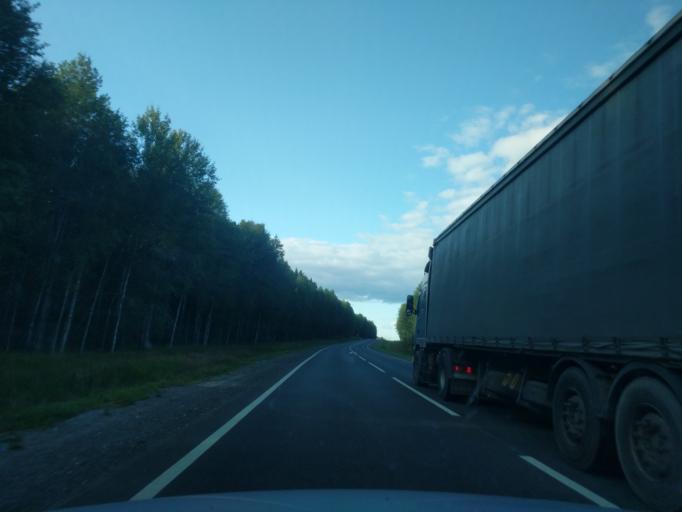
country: RU
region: Kostroma
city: Manturovo
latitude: 58.3151
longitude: 44.7190
